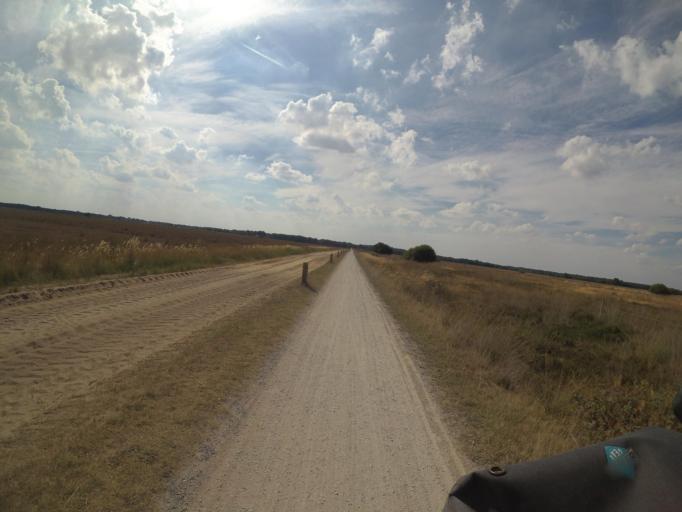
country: NL
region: Drenthe
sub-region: Gemeente De Wolden
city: Ruinen
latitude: 52.7914
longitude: 6.3884
